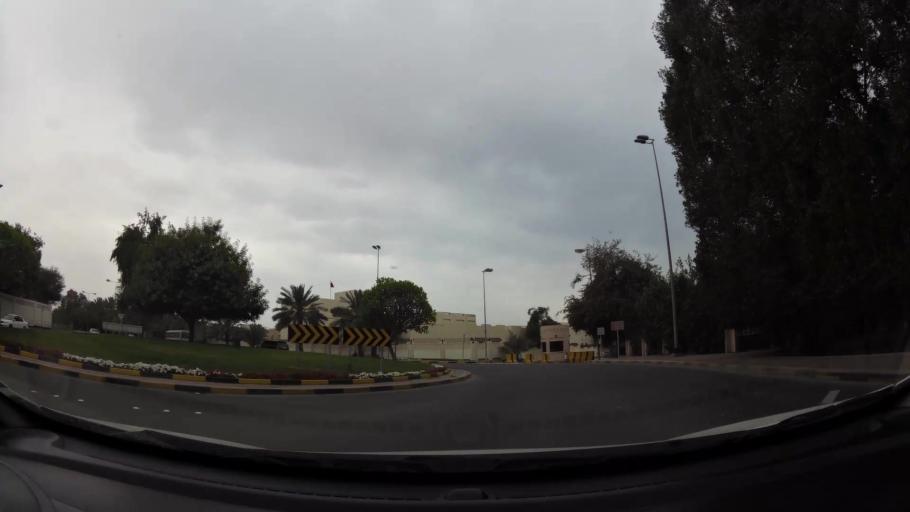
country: BH
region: Northern
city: Ar Rifa'
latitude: 26.1245
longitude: 50.5354
